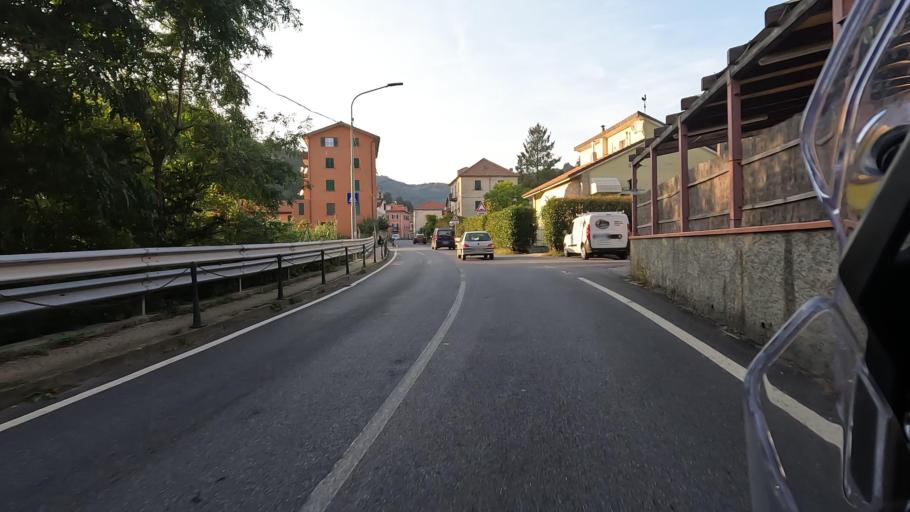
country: IT
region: Liguria
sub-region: Provincia di Savona
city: Osteria dei Cacciatori-Stella
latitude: 44.4162
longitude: 8.4825
